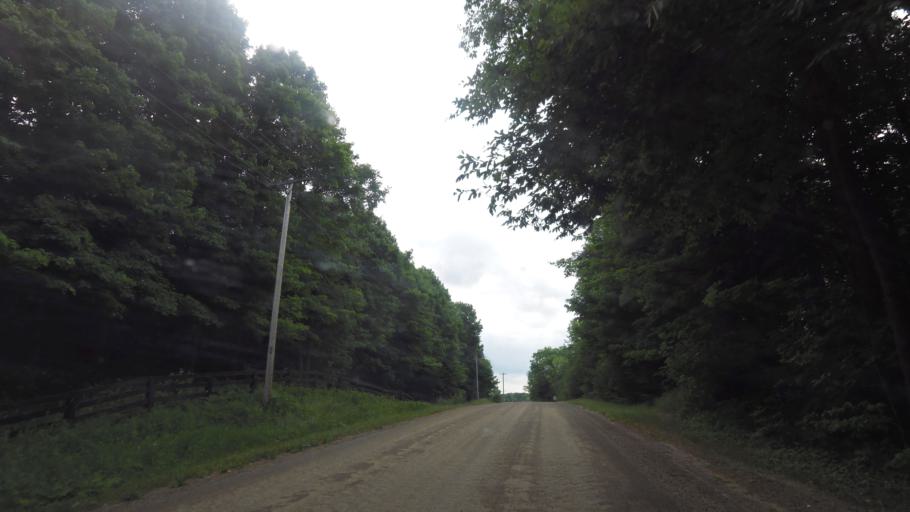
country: CA
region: Ontario
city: Orangeville
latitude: 43.8657
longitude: -79.9411
